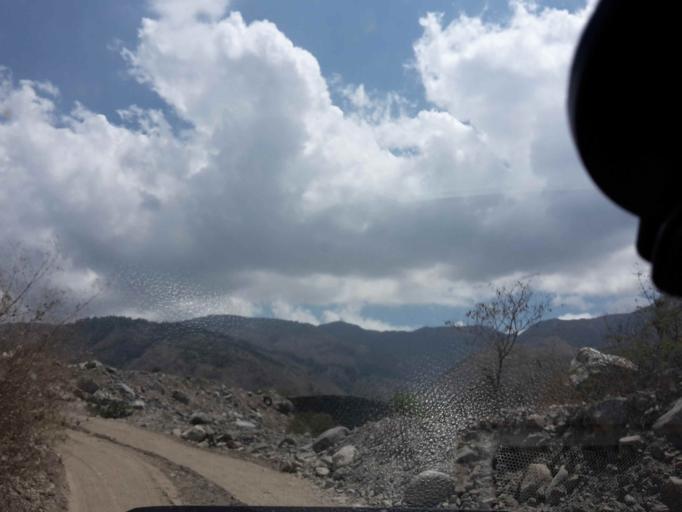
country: BO
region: Cochabamba
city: Cochabamba
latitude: -17.3314
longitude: -66.2117
